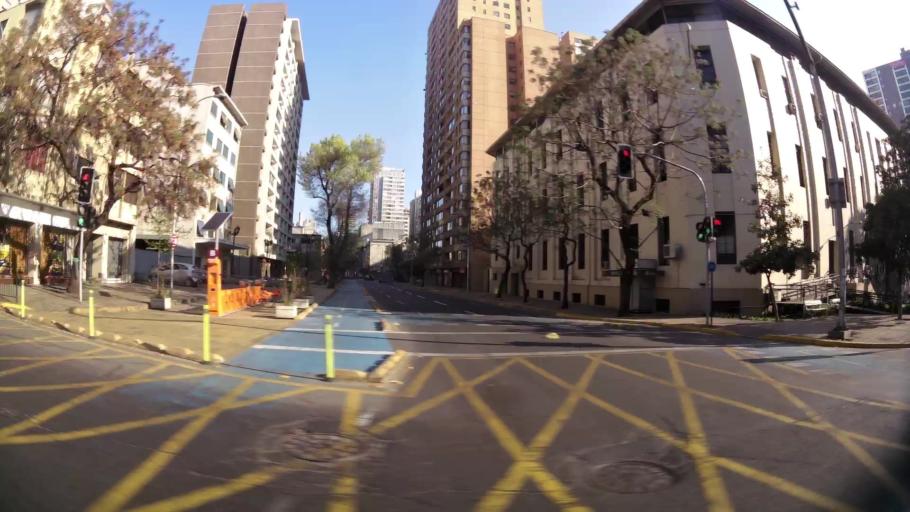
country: CL
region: Santiago Metropolitan
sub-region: Provincia de Santiago
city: Santiago
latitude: -33.4332
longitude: -70.6559
